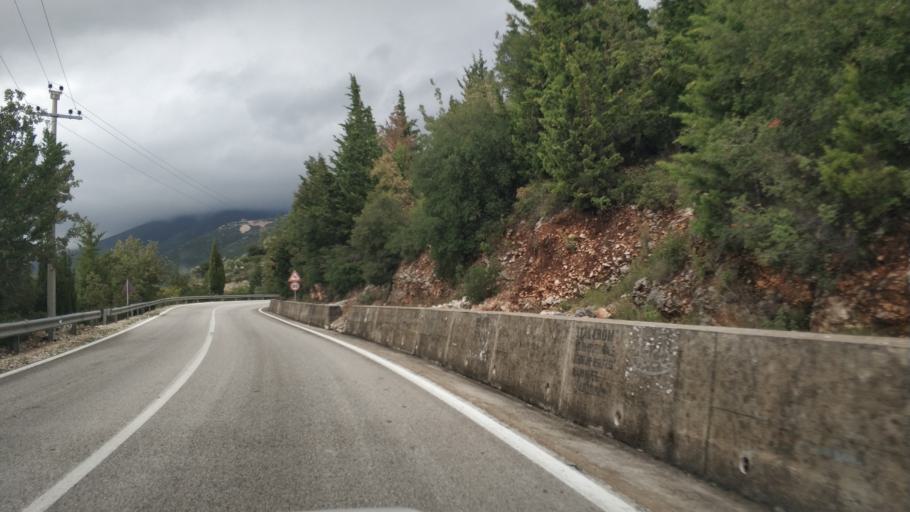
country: AL
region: Vlore
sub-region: Rrethi i Vlores
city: Vranisht
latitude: 40.1691
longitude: 19.6176
